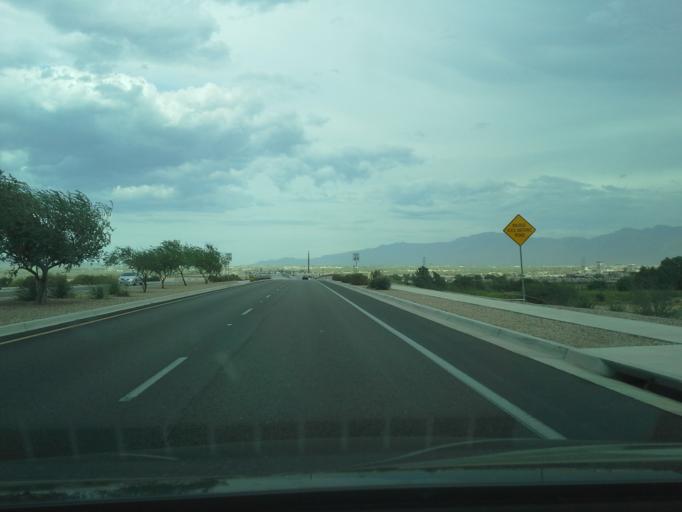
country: US
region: Arizona
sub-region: Pima County
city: Tortolita
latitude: 32.3750
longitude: -111.1172
